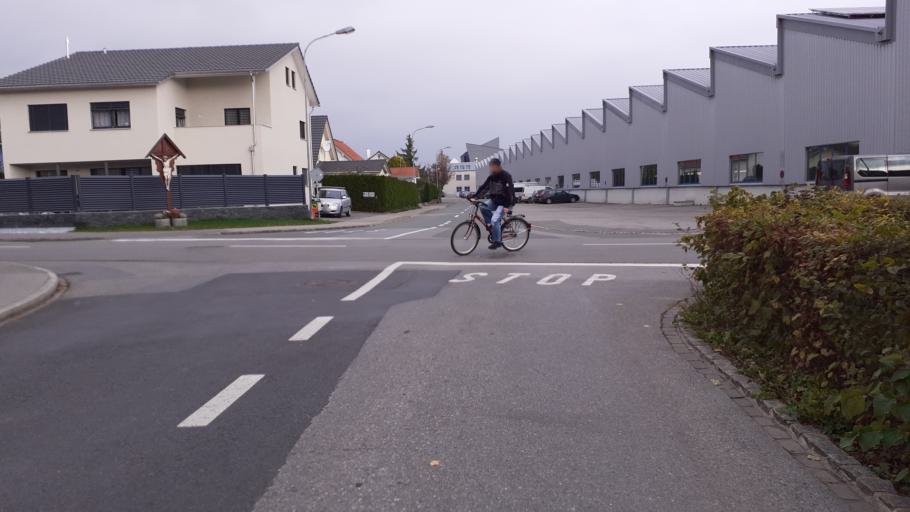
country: CH
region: Saint Gallen
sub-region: Wahlkreis Rheintal
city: Oberriet
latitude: 47.3176
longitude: 9.5679
